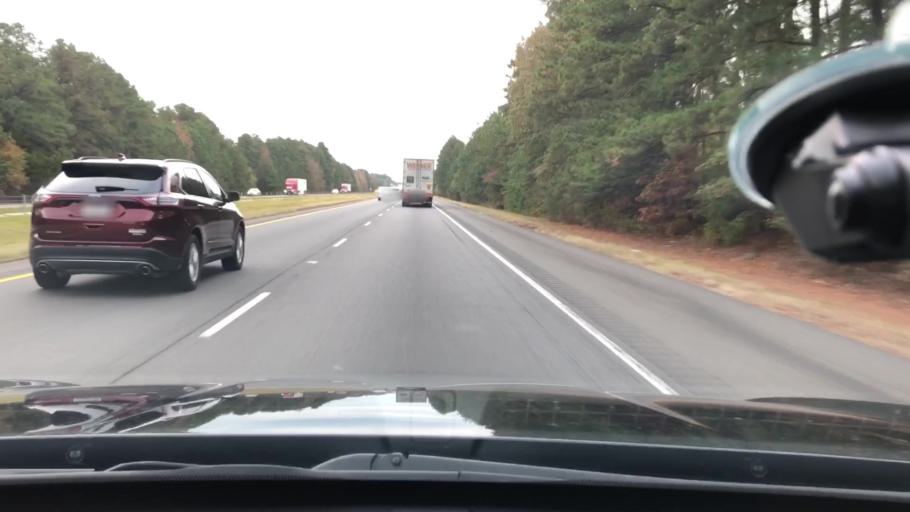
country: US
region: Arkansas
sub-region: Clark County
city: Arkadelphia
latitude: 34.0597
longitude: -93.1284
